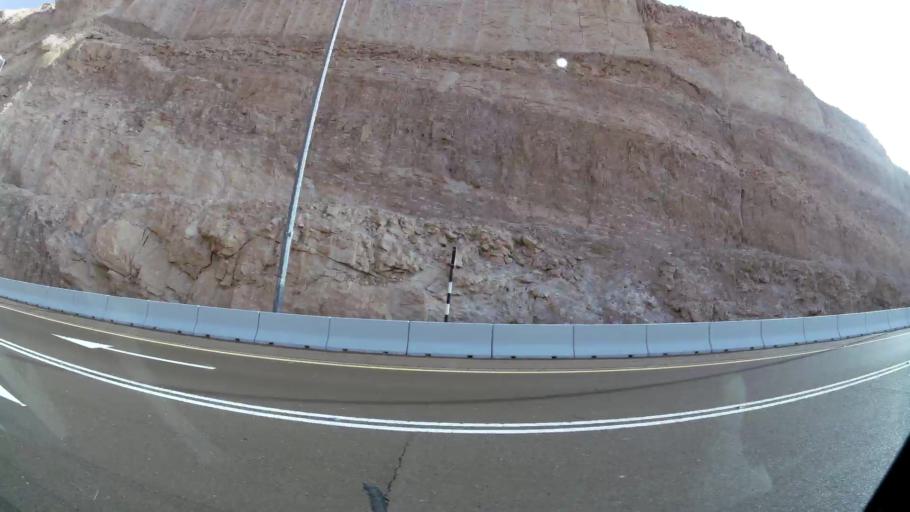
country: AE
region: Abu Dhabi
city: Al Ain
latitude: 24.0960
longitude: 55.7576
